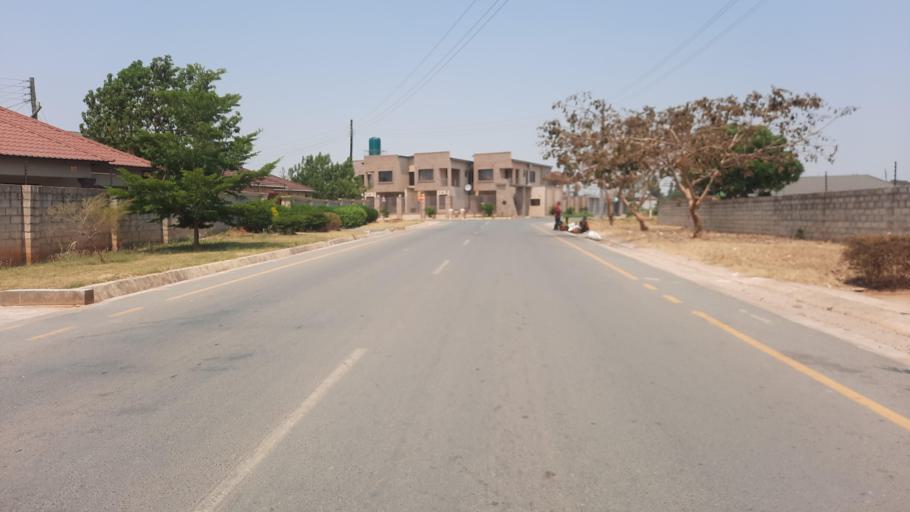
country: ZM
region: Lusaka
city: Lusaka
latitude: -15.3953
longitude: 28.3903
